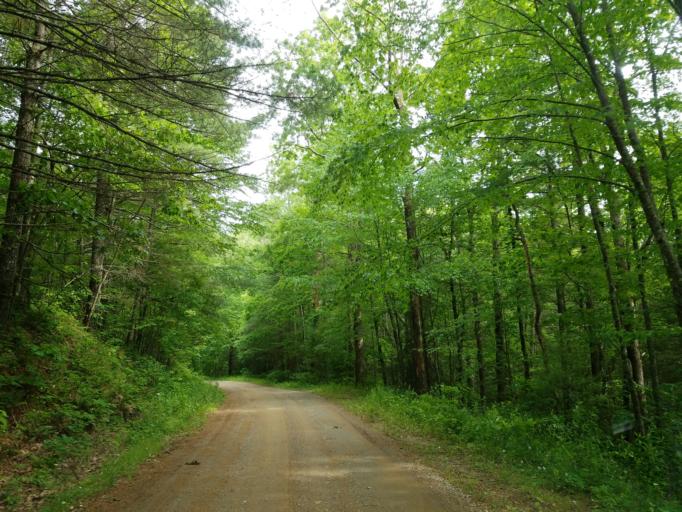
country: US
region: Georgia
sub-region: Union County
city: Blairsville
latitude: 34.7571
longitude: -84.0027
